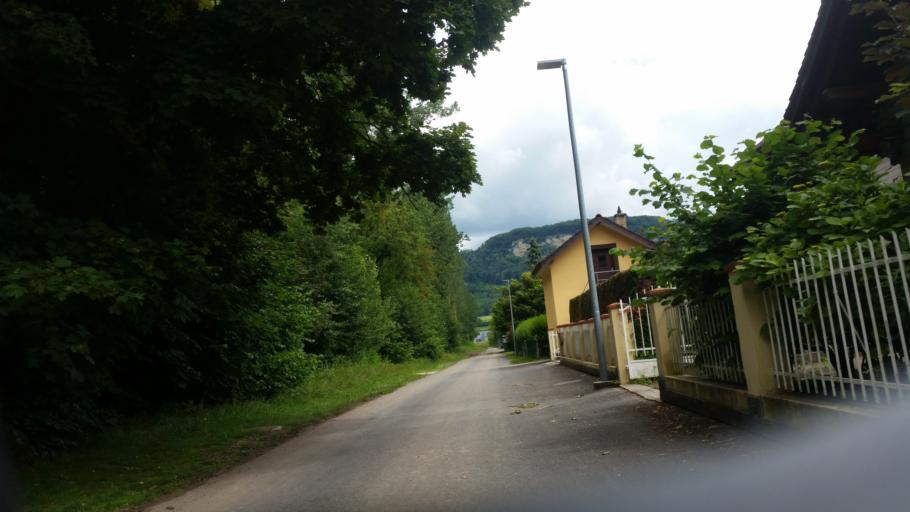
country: CH
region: Vaud
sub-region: Jura-Nord vaudois District
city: Yvonand
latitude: 46.8015
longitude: 6.7470
